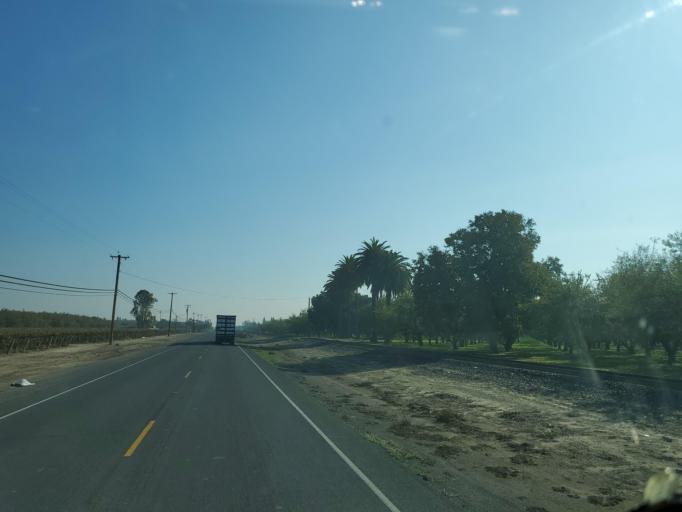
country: US
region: California
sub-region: San Joaquin County
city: Manteca
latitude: 37.8507
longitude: -121.1932
